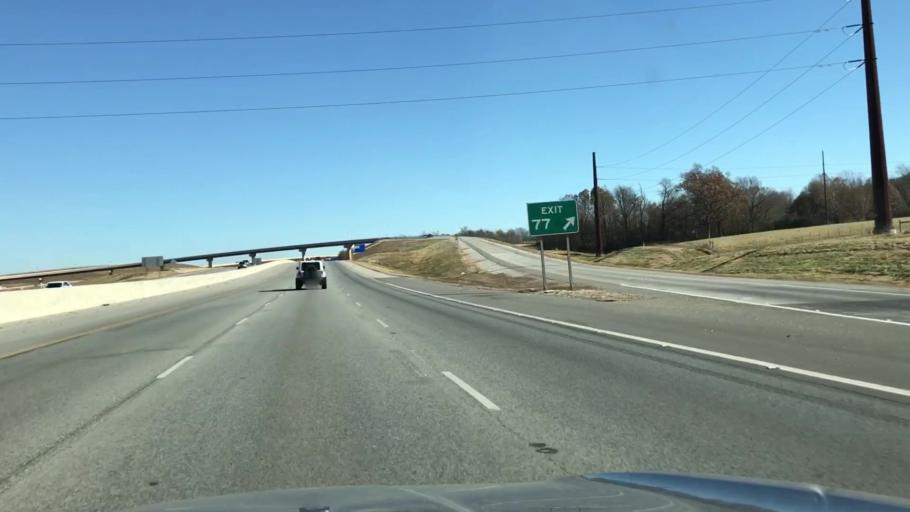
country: US
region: Arkansas
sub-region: Benton County
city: Lowell
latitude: 36.2349
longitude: -94.1672
